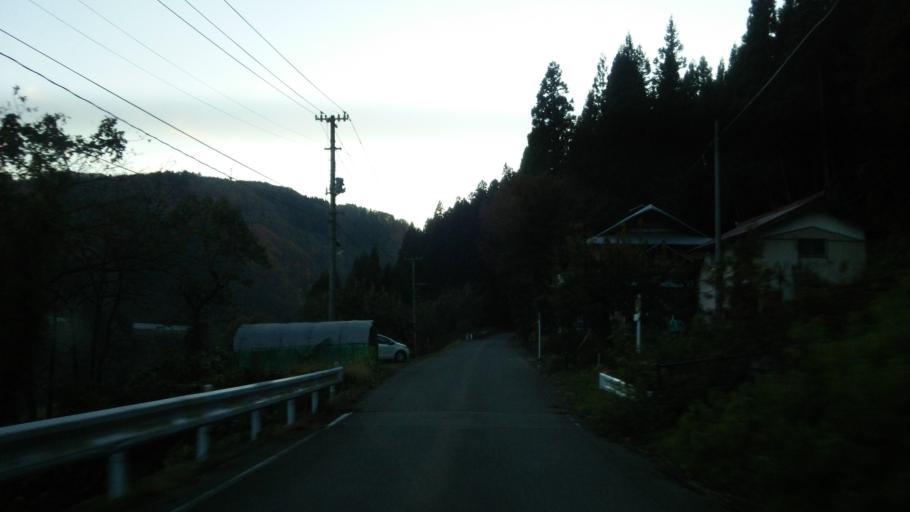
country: JP
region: Fukushima
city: Kitakata
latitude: 37.5111
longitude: 139.7005
